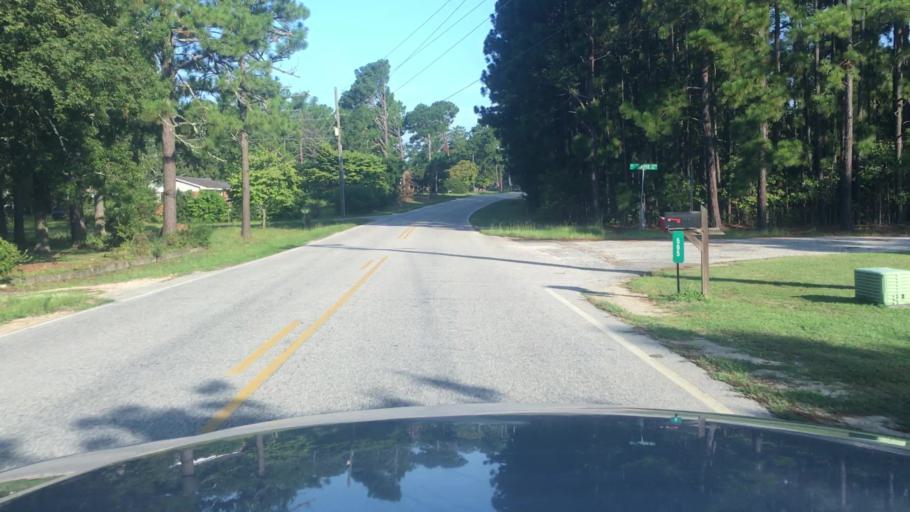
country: US
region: North Carolina
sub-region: Harnett County
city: Walkertown
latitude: 35.2109
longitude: -78.8615
